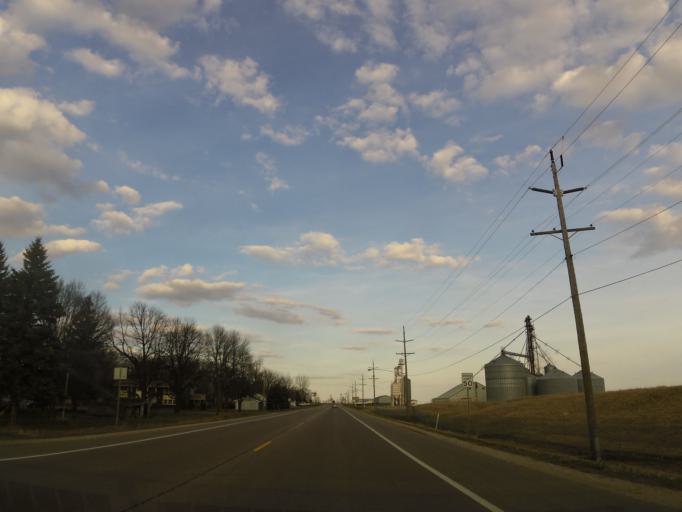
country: US
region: Minnesota
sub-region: McLeod County
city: Hutchinson
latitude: 44.7204
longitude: -94.4871
